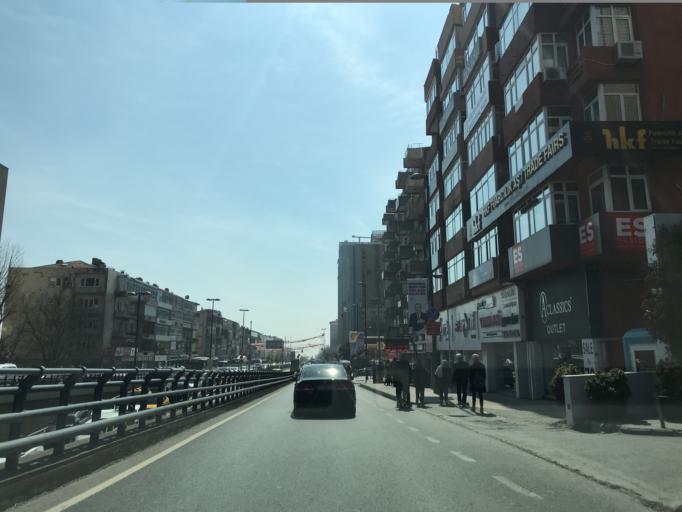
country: TR
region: Istanbul
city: Sisli
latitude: 41.0624
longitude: 29.0114
